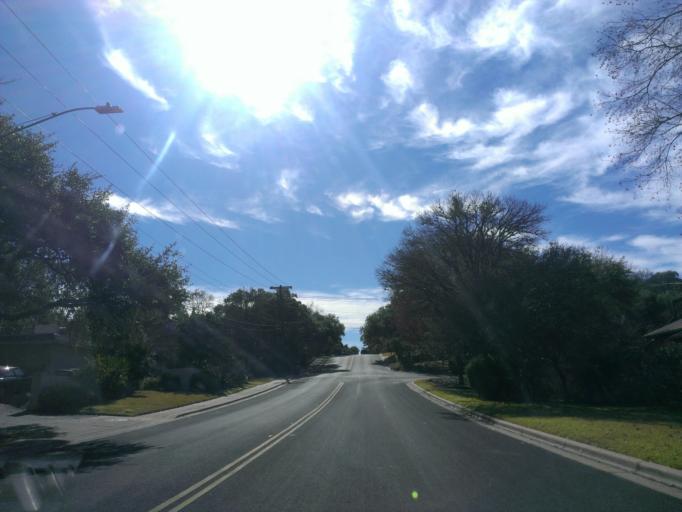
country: US
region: Texas
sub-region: Travis County
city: West Lake Hills
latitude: 30.3106
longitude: -97.7678
